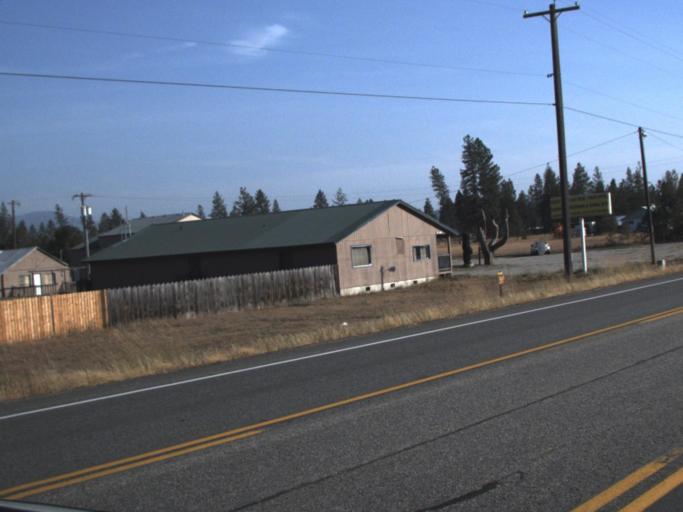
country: US
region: Washington
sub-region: Spokane County
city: Deer Park
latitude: 48.0212
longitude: -117.3497
